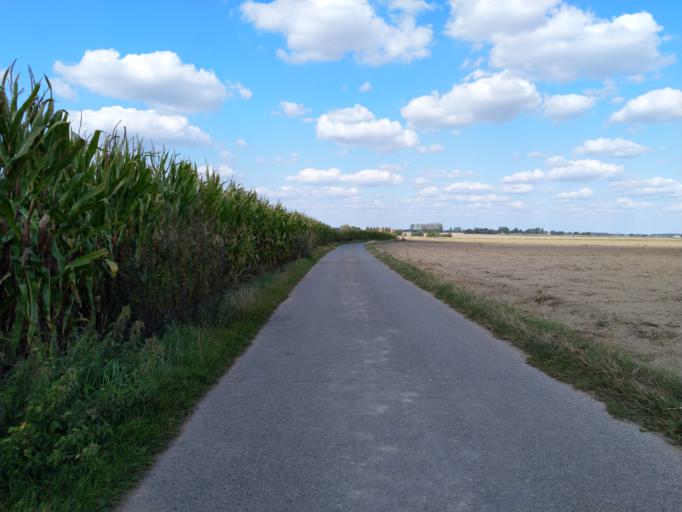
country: BE
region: Wallonia
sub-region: Province du Hainaut
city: Saint-Ghislain
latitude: 50.5115
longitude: 3.8193
